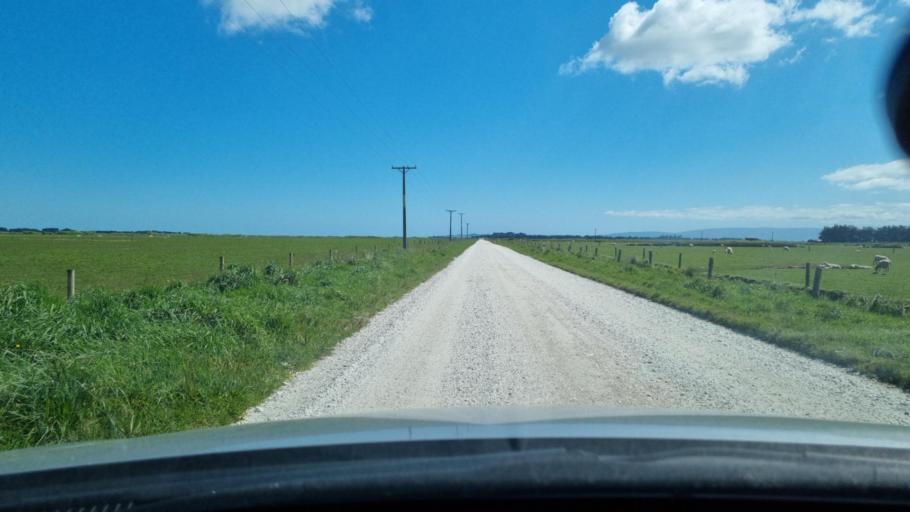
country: NZ
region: Southland
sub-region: Invercargill City
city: Invercargill
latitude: -46.3693
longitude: 168.2643
